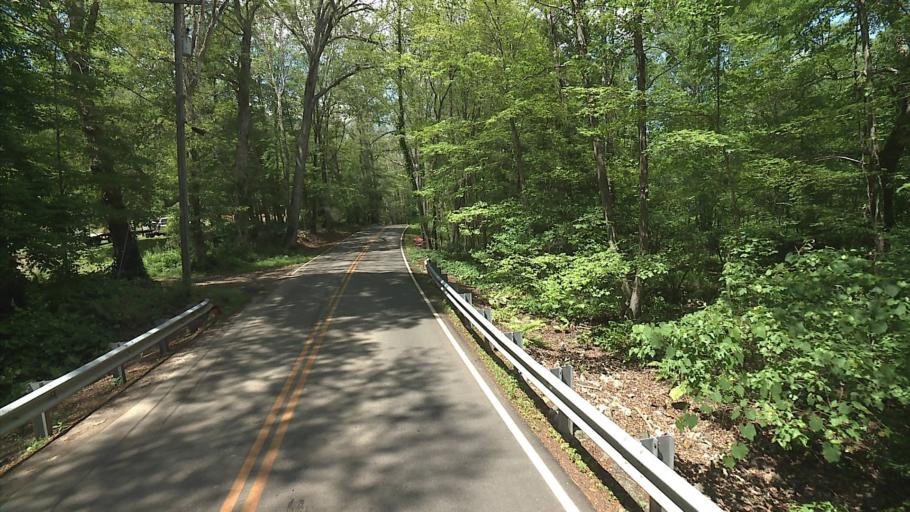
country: US
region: Connecticut
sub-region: New London County
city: Colchester
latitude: 41.4681
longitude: -72.3381
